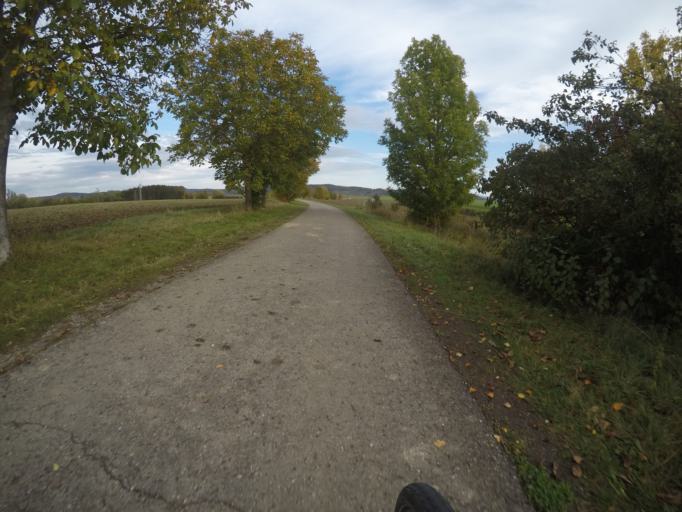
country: DE
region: Baden-Wuerttemberg
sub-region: Tuebingen Region
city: Rottenburg
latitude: 48.5417
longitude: 8.9342
